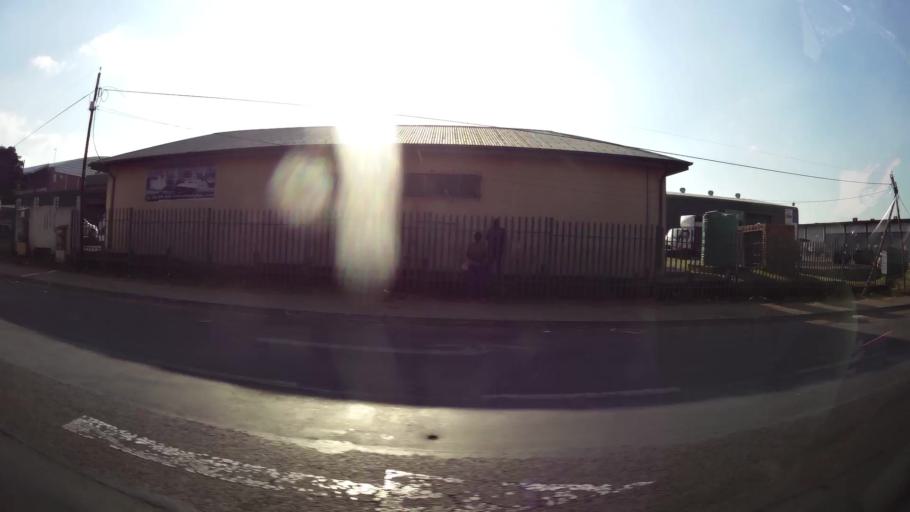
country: ZA
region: Gauteng
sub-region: City of Johannesburg Metropolitan Municipality
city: Modderfontein
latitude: -26.0948
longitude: 28.2613
